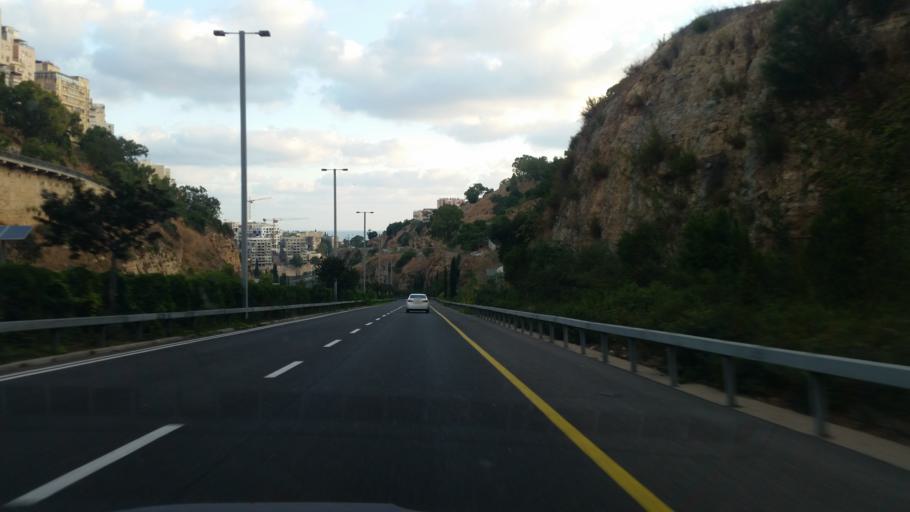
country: IL
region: Haifa
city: Haifa
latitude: 32.7959
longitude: 35.0046
